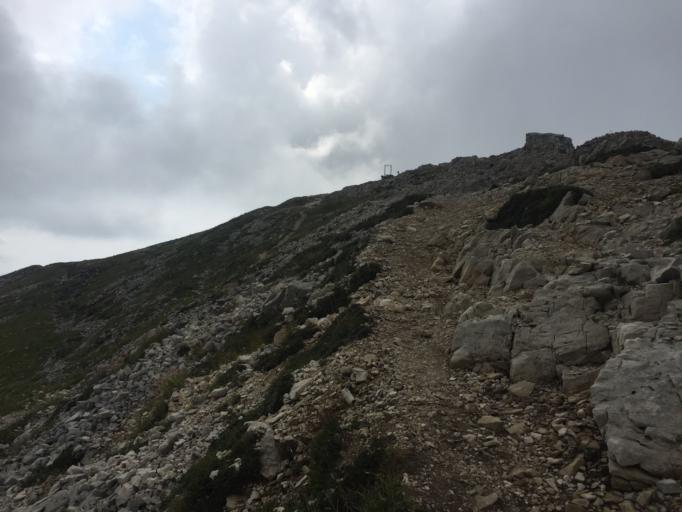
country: IT
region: Trentino-Alto Adige
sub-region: Provincia di Trento
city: Vallarsa
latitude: 45.7930
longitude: 11.1765
